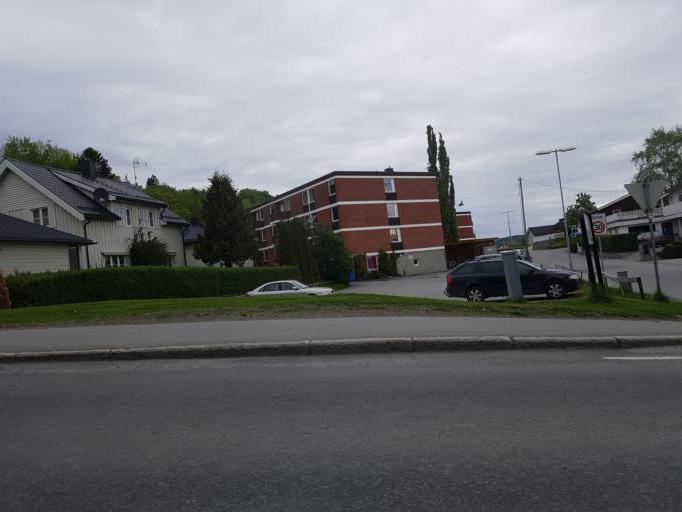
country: NO
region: Nord-Trondelag
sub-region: Levanger
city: Levanger
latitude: 63.7474
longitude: 11.2913
